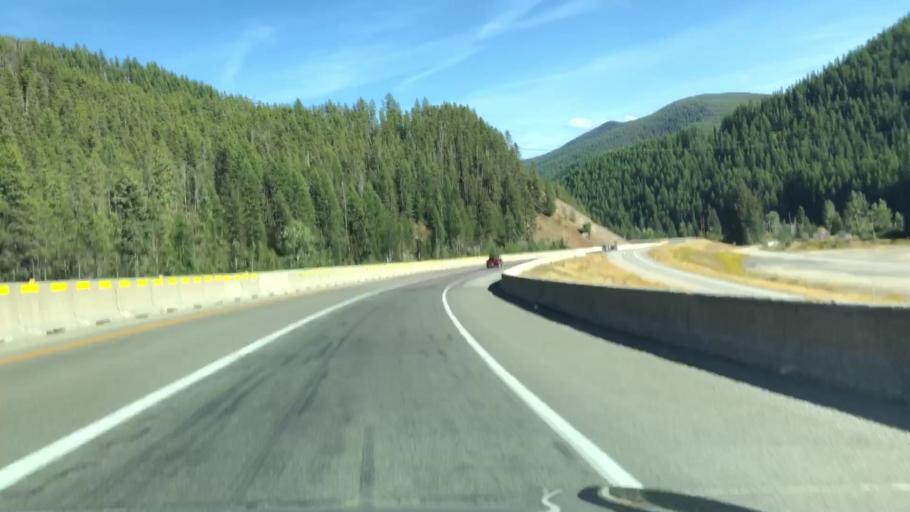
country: US
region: Montana
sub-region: Sanders County
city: Thompson Falls
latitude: 47.4219
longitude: -115.6069
